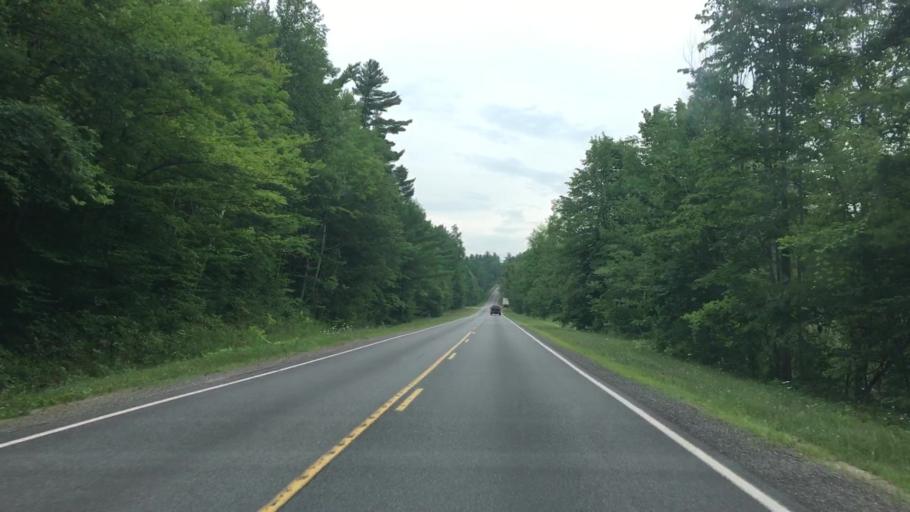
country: US
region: New York
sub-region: Clinton County
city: Peru
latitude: 44.4977
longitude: -73.5913
